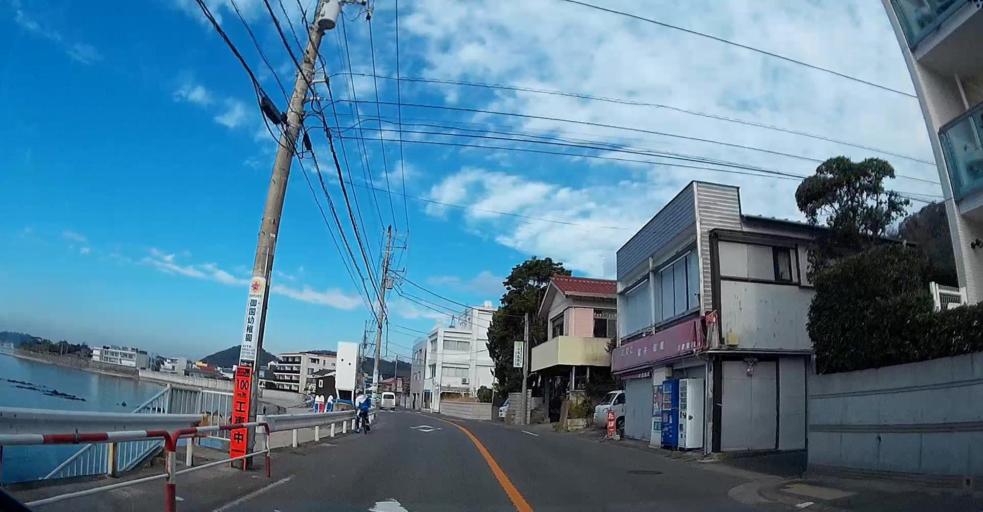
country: JP
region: Kanagawa
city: Hayama
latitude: 35.2692
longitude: 139.5708
